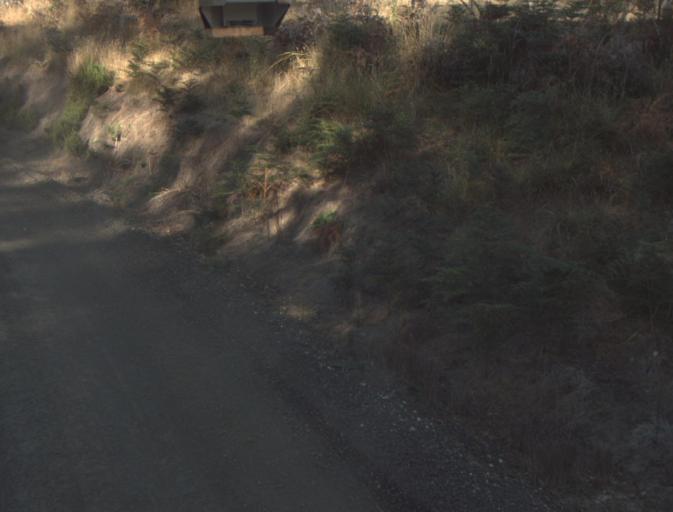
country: AU
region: Tasmania
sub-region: Launceston
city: Mayfield
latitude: -41.2962
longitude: 147.1983
